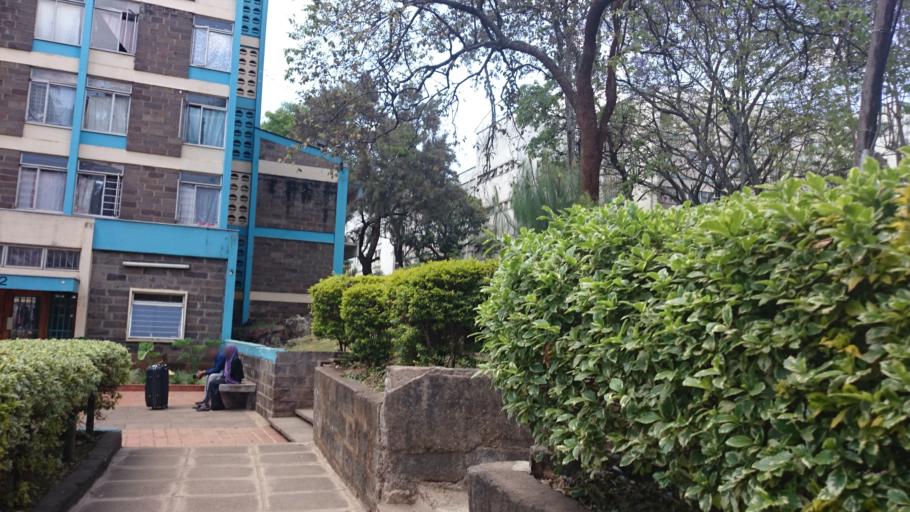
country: KE
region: Nairobi Area
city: Nairobi
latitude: -1.2825
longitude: 36.8128
